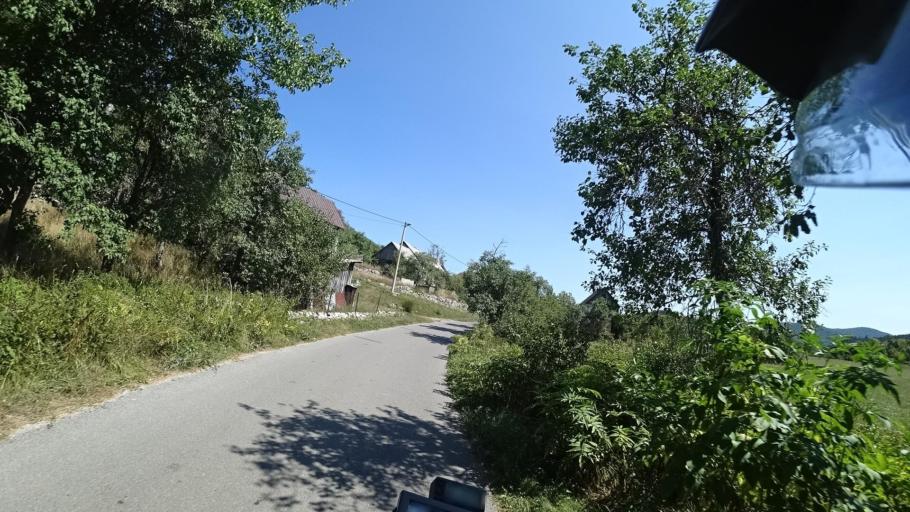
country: HR
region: Licko-Senjska
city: Popovaca
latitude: 44.7164
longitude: 15.2725
